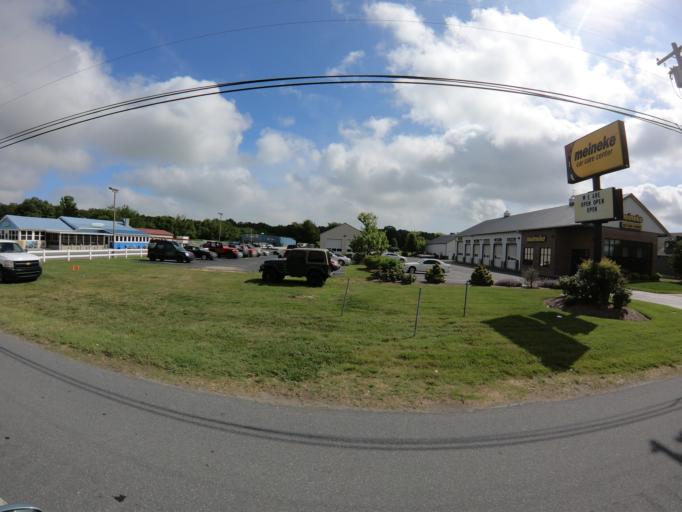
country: US
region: Delaware
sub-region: Sussex County
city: Lewes
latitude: 38.7567
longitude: -75.1960
